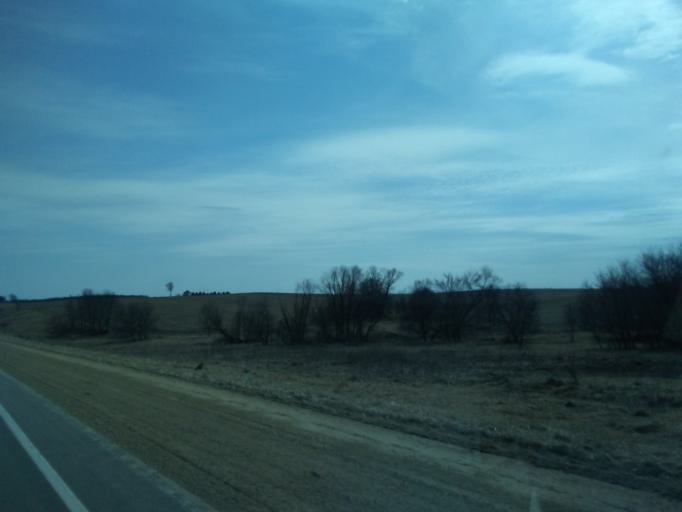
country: US
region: Iowa
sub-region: Winneshiek County
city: Decorah
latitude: 43.3795
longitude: -91.8190
